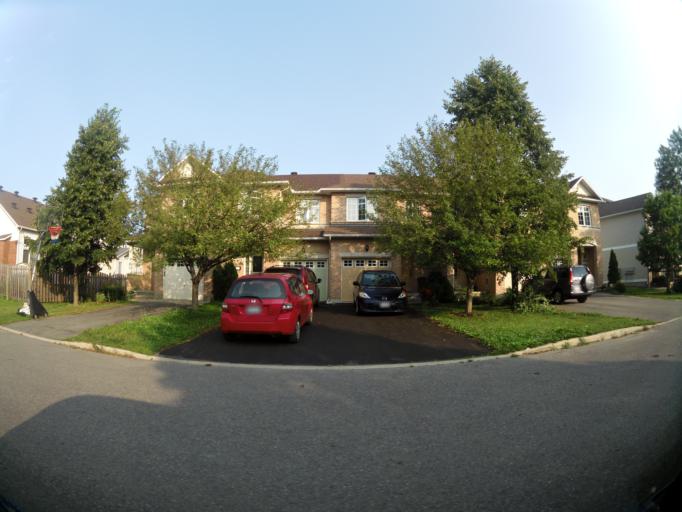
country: CA
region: Ontario
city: Clarence-Rockland
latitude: 45.4799
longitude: -75.4627
